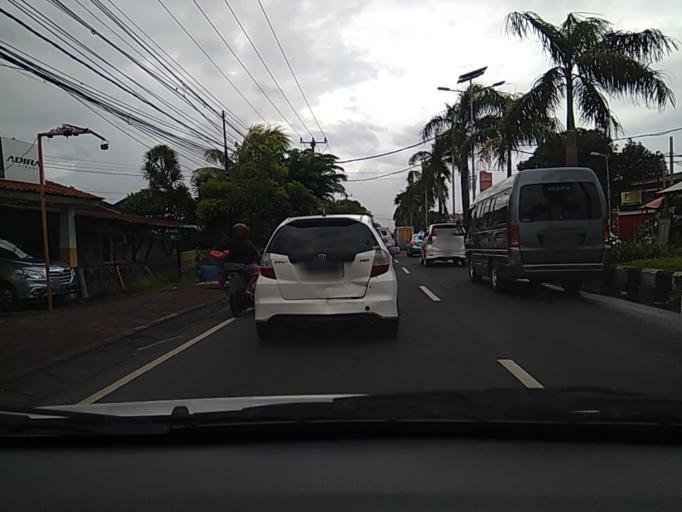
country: ID
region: Bali
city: Kelanabian
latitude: -8.7708
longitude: 115.1778
